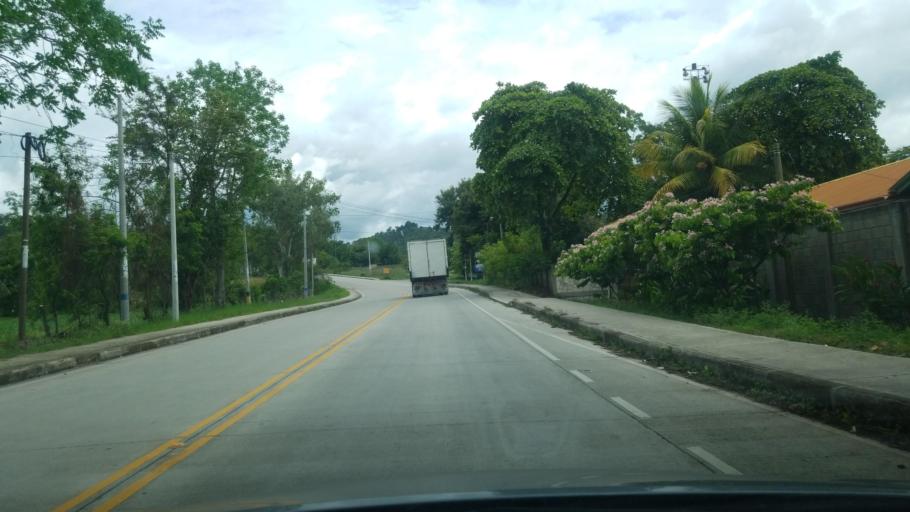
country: HN
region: Copan
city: Florida
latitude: 15.0297
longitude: -88.8312
